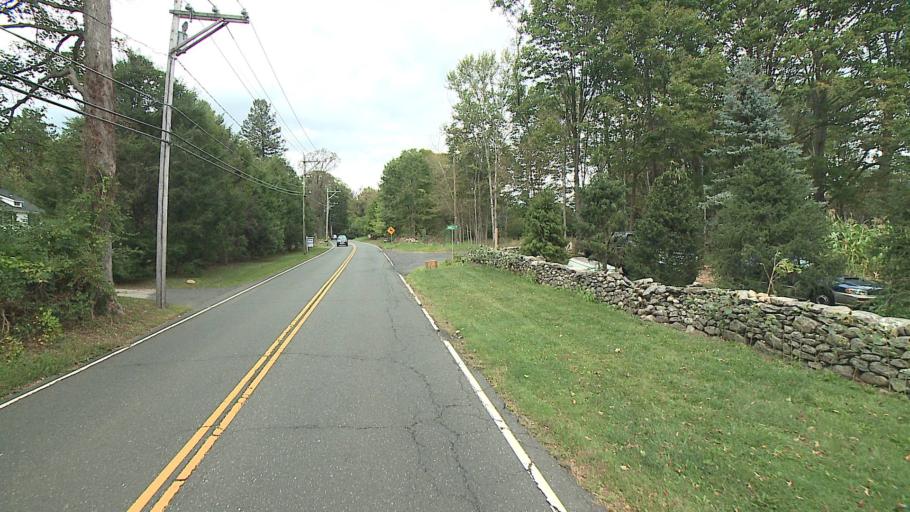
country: US
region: Connecticut
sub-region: Fairfield County
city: Ridgefield
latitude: 41.2525
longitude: -73.4911
